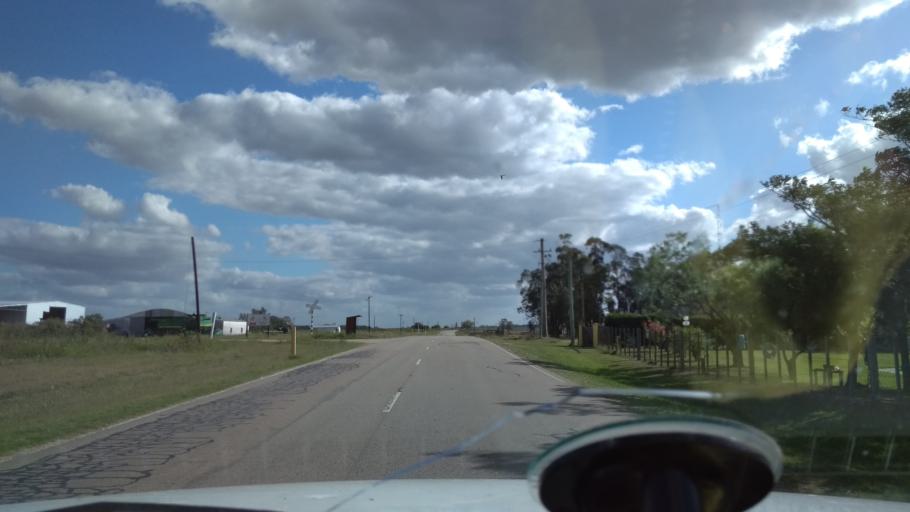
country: UY
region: Florida
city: Casupa
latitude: -34.1490
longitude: -55.6818
